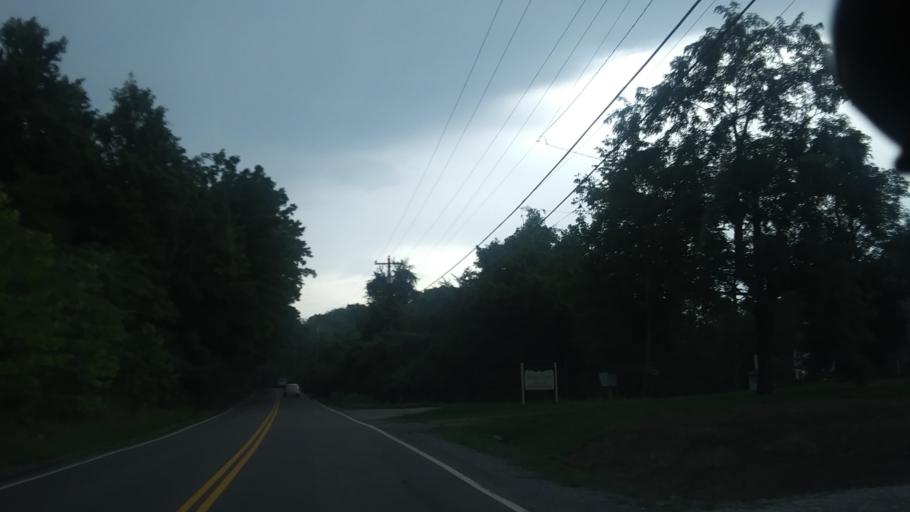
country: US
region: Tennessee
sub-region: Davidson County
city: Belle Meade
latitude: 36.0908
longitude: -86.9344
